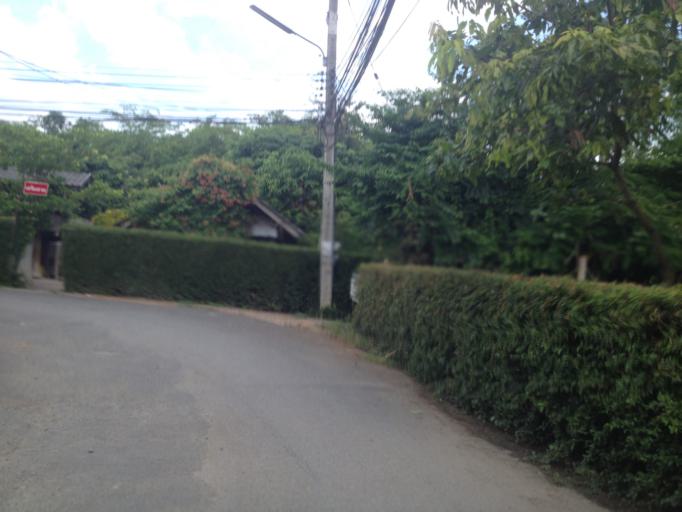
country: TH
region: Chiang Mai
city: Hang Dong
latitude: 18.7133
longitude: 98.9301
